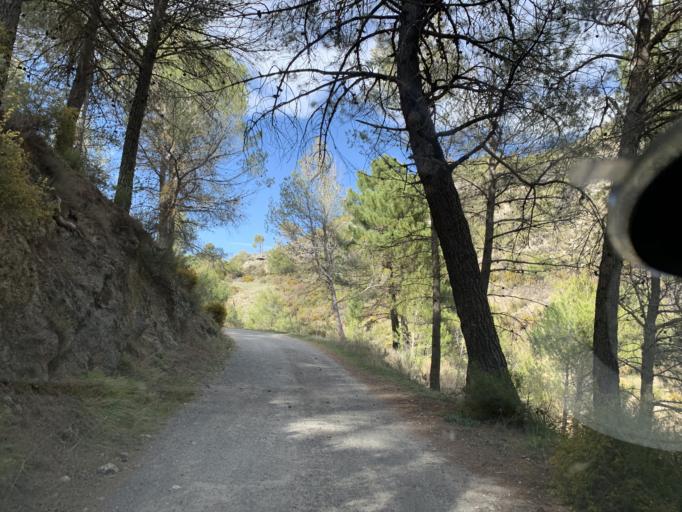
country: ES
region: Andalusia
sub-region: Provincia de Granada
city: Quentar
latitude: 37.2279
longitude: -3.4091
